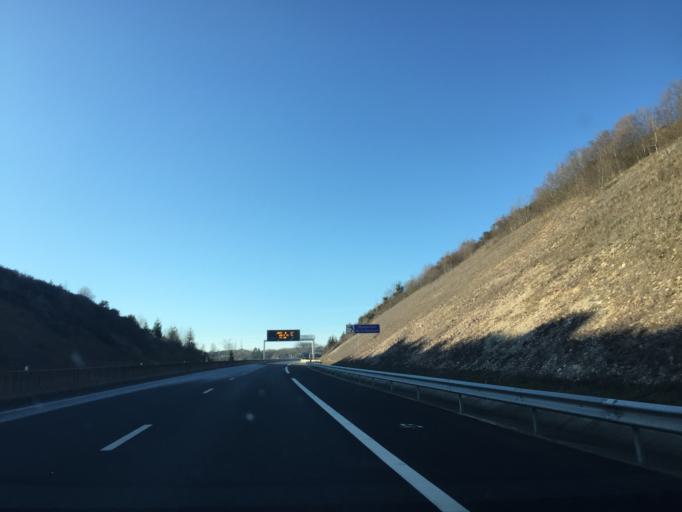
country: FR
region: Limousin
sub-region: Departement de la Correze
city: Cublac
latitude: 45.1653
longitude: 1.2529
